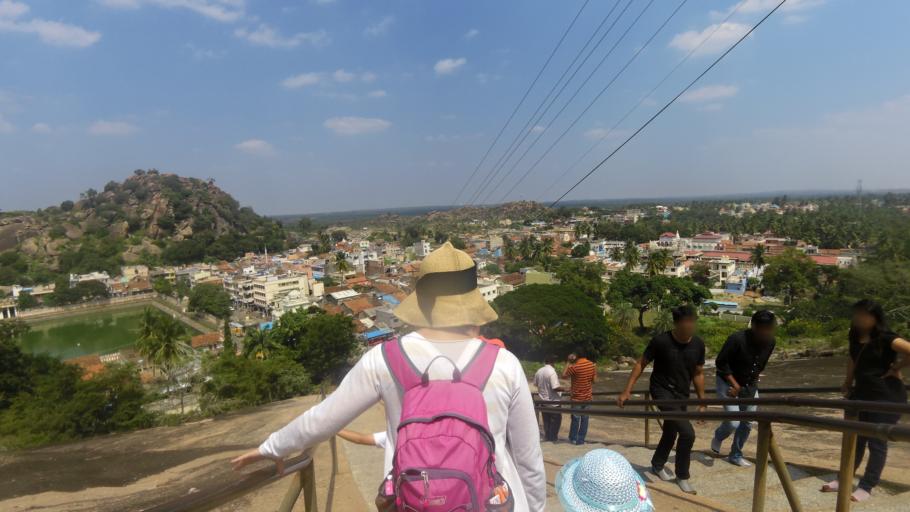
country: IN
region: Karnataka
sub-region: Hassan
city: Shravanabelagola
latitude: 12.8561
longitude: 76.4863
